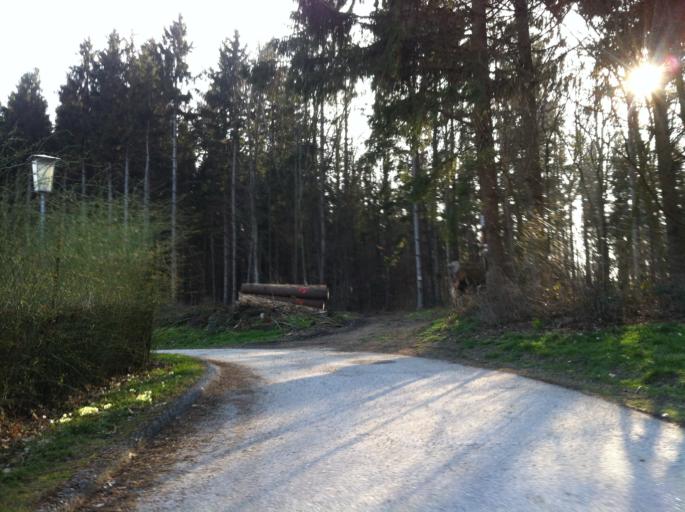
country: AT
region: Lower Austria
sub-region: Politischer Bezirk Wien-Umgebung
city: Pressbaum
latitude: 48.1799
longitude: 16.1044
